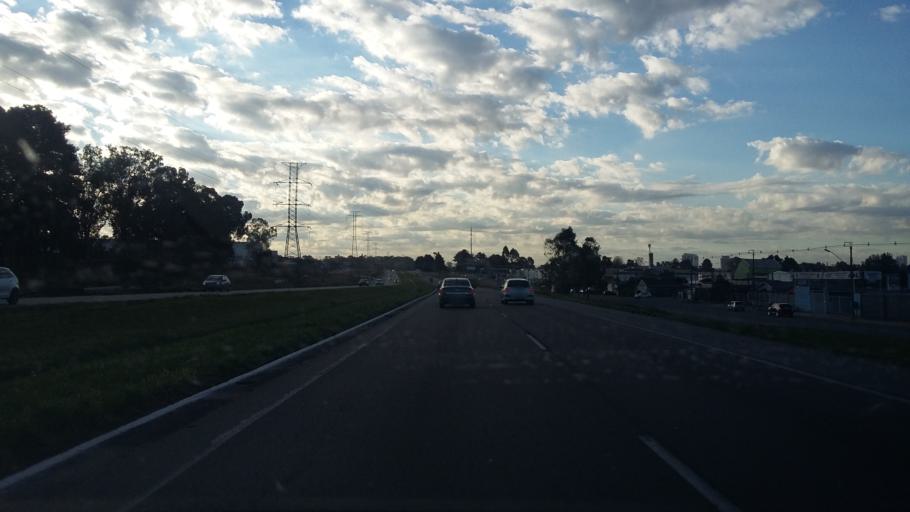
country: BR
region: Parana
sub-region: Curitiba
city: Curitiba
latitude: -25.4766
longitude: -49.3509
